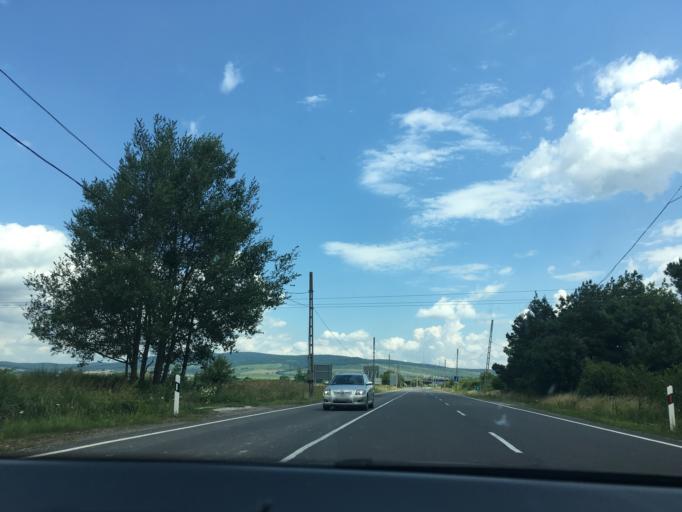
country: HU
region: Borsod-Abauj-Zemplen
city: Satoraljaujhely
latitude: 48.4214
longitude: 21.6476
